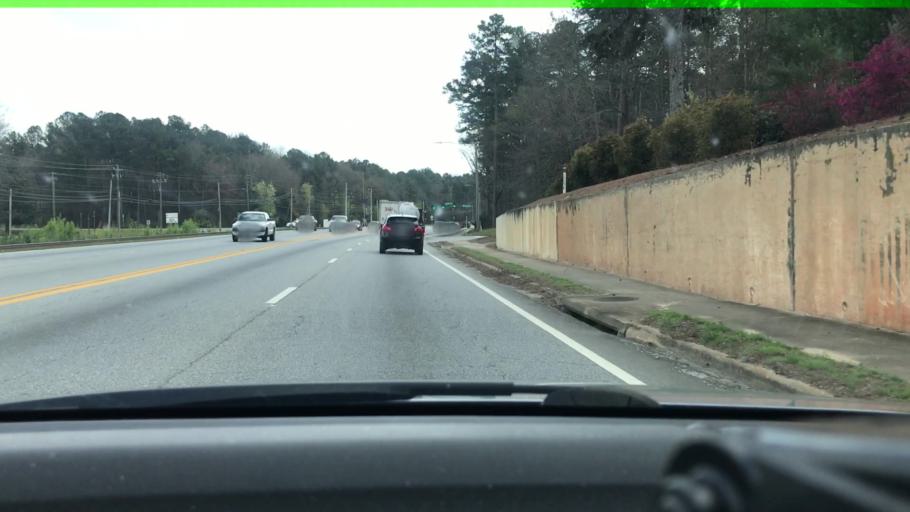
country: US
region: Georgia
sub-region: Clarke County
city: Country Club Estates
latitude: 33.9841
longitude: -83.4182
